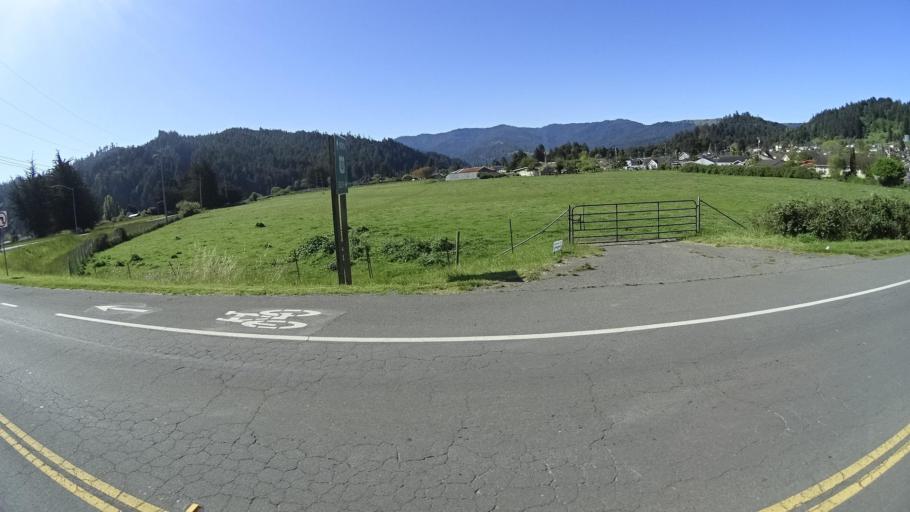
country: US
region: California
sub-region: Humboldt County
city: Rio Dell
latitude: 40.4992
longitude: -124.1009
